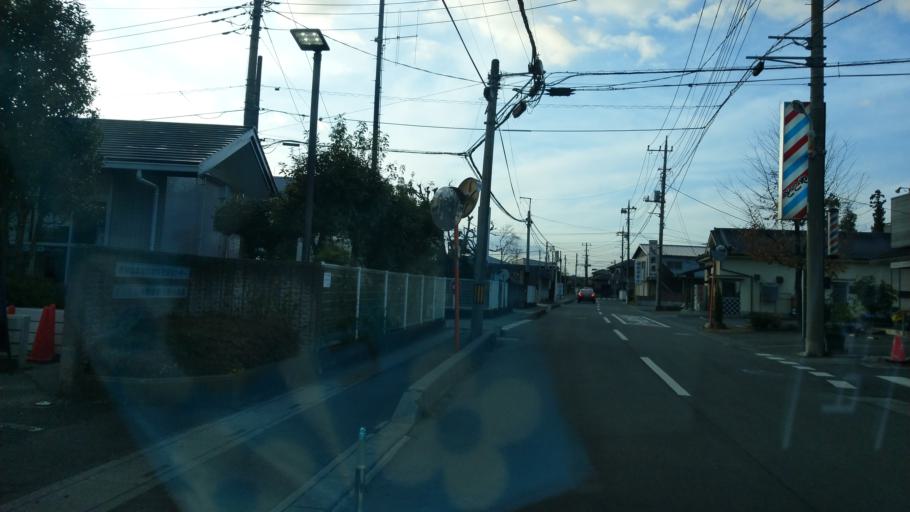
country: JP
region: Saitama
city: Yono
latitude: 35.8939
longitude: 139.5924
